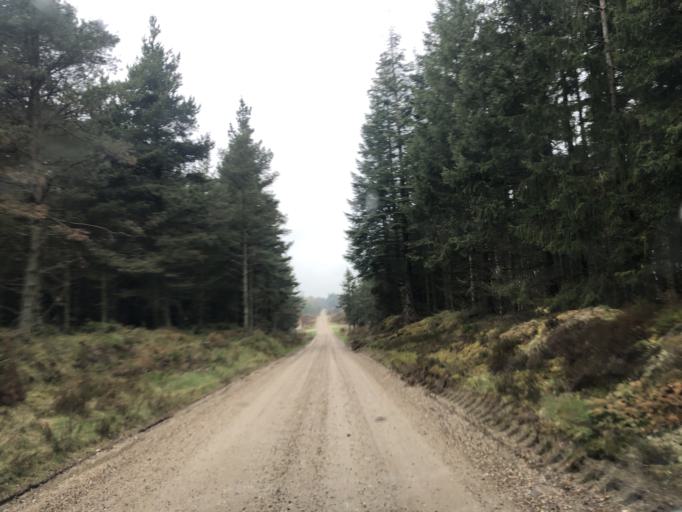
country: DK
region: Central Jutland
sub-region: Lemvig Kommune
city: Lemvig
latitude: 56.4709
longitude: 8.3847
